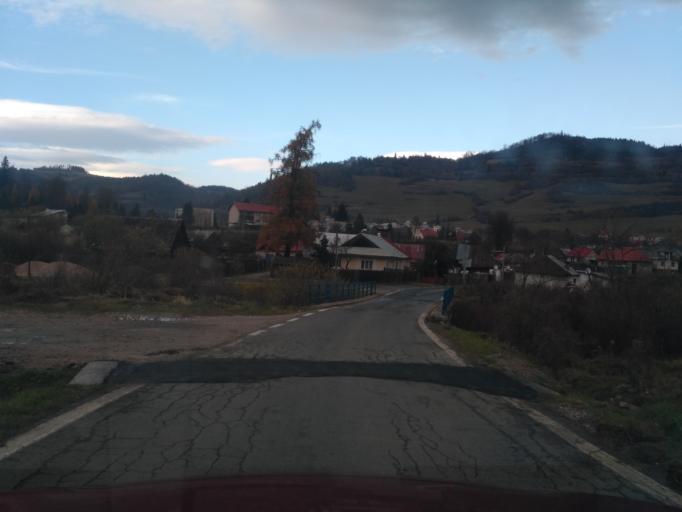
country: SK
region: Kosicky
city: Spisska Nova Ves
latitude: 48.8372
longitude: 20.6179
